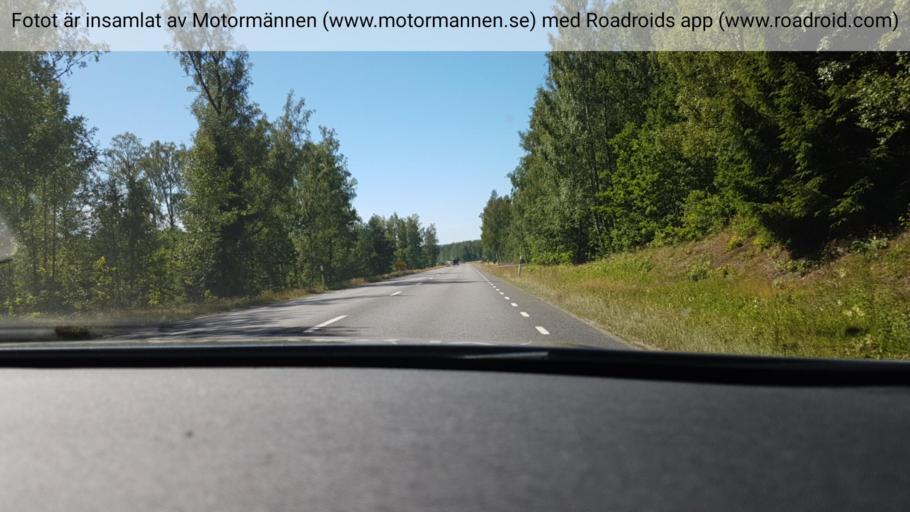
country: SE
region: Joenkoeping
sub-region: Habo Kommun
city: Habo
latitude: 57.9732
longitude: 14.1051
